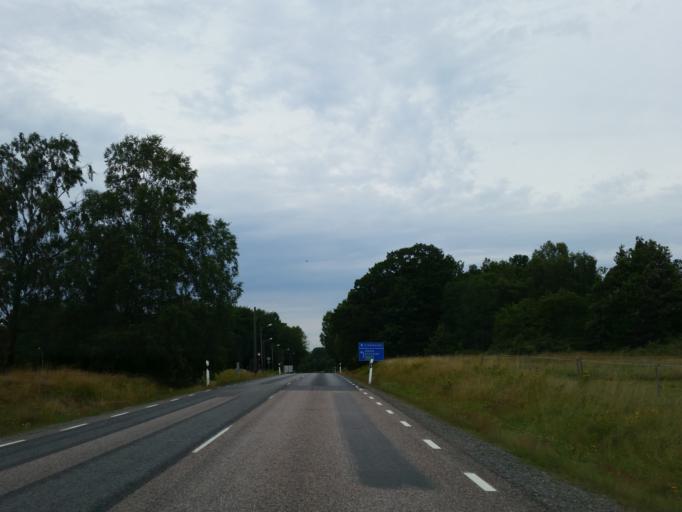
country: SE
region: Stockholm
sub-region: Nykvarns Kommun
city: Nykvarn
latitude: 59.1908
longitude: 17.4625
